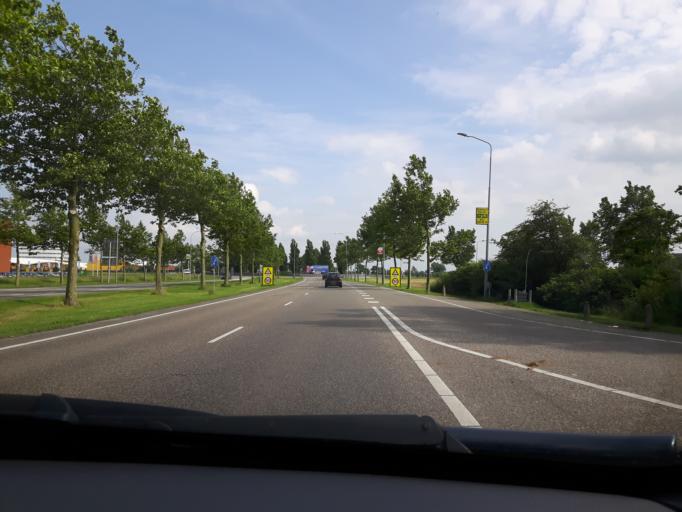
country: NL
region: Zeeland
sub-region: Gemeente Middelburg
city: Middelburg
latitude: 51.4825
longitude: 3.6263
